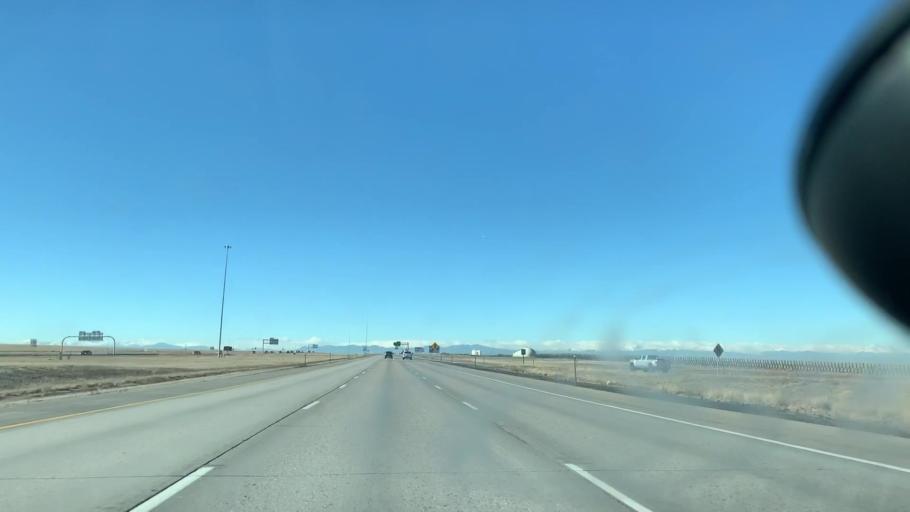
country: US
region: Colorado
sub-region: Adams County
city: Aurora
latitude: 39.8346
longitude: -104.7524
